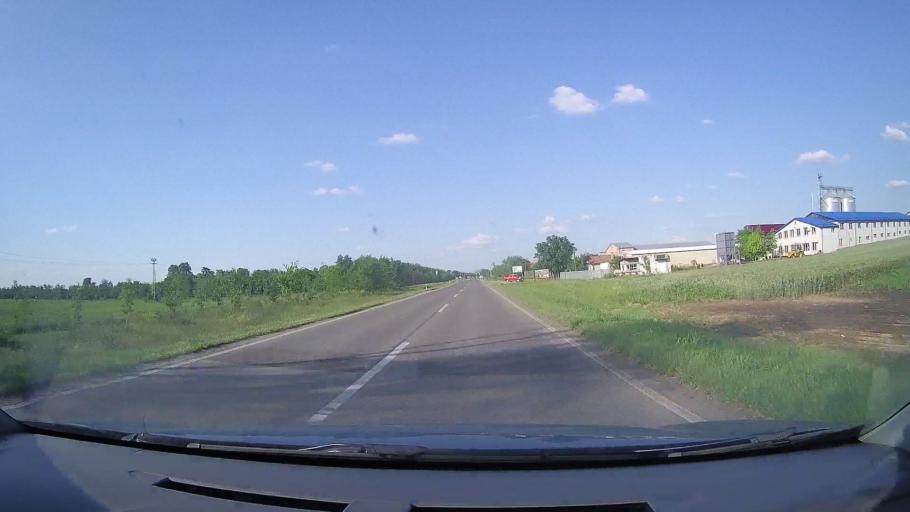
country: RS
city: Vladimirovac
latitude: 44.9757
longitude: 20.7669
